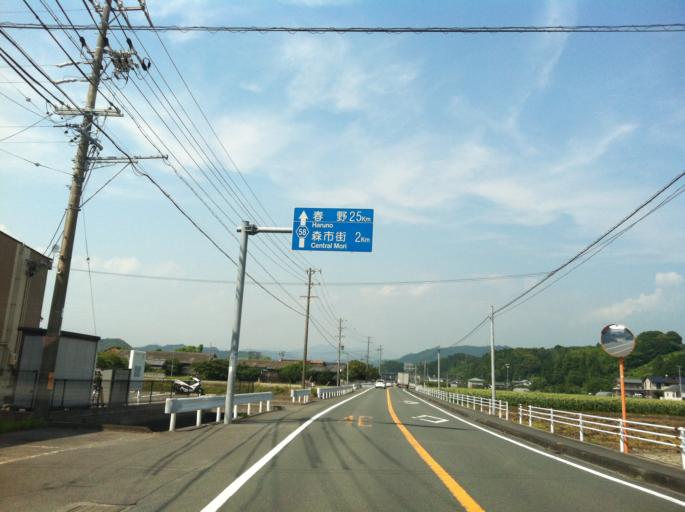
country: JP
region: Shizuoka
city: Mori
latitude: 34.8250
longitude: 137.9260
